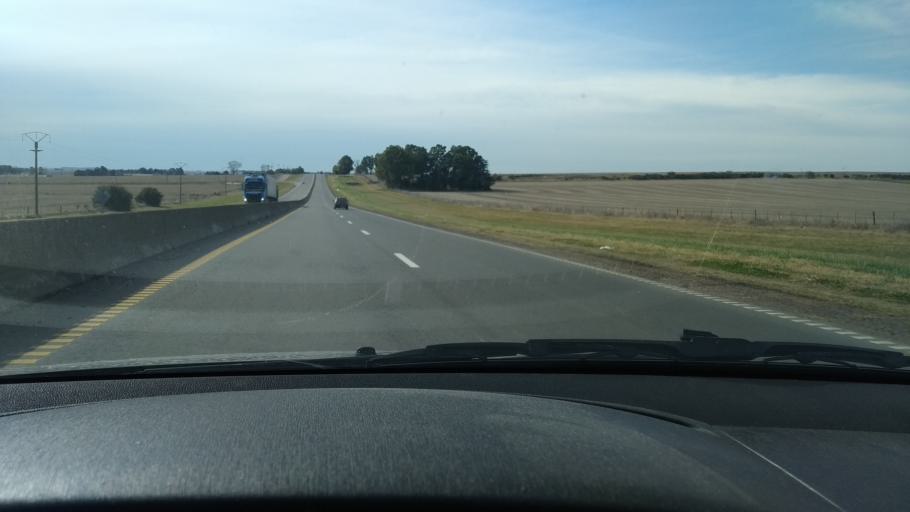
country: AR
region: Buenos Aires
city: Olavarria
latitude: -36.8966
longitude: -60.1672
